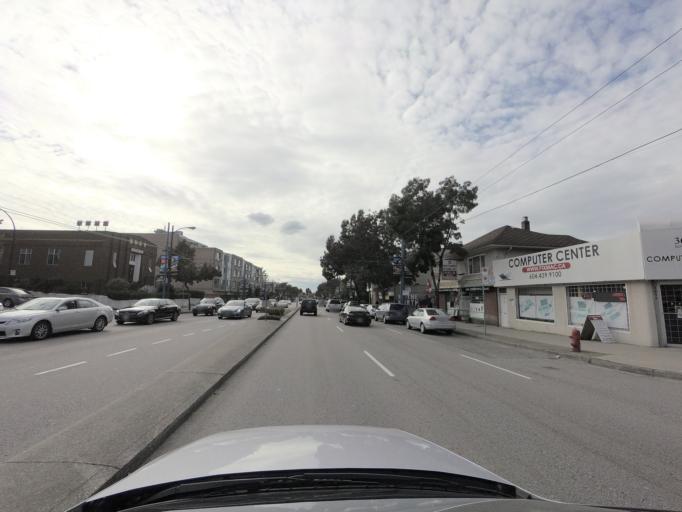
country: CA
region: British Columbia
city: Burnaby
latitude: 49.2321
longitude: -123.0271
